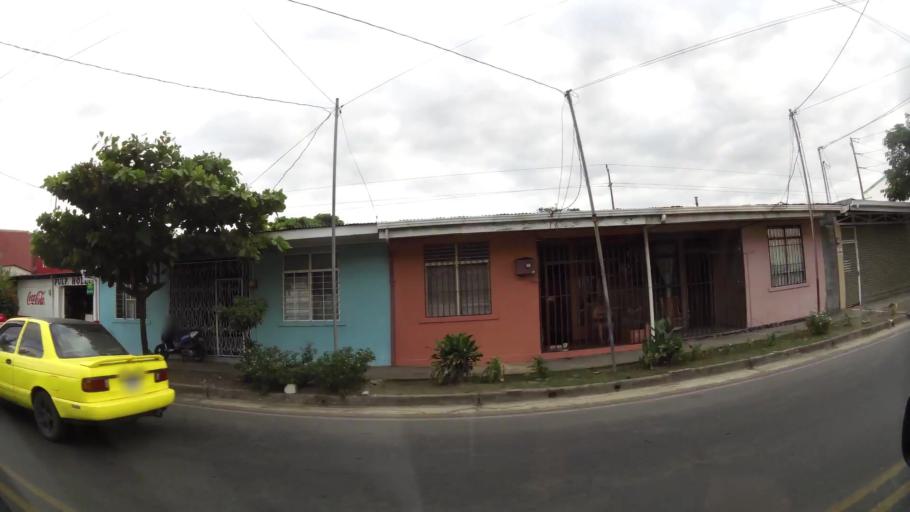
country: CR
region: Puntarenas
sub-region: Canton Central de Puntarenas
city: Puntarenas
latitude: 9.9792
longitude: -84.8205
